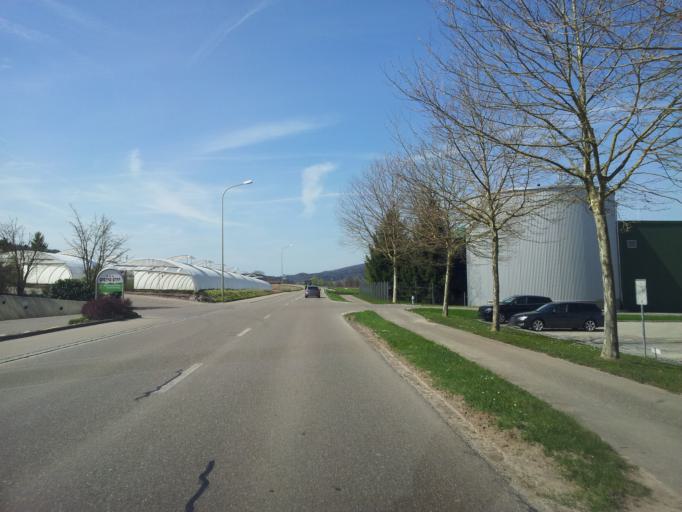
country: CH
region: Zurich
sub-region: Bezirk Dielsdorf
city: Daellikon / Daellikon (Dorf)
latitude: 47.4411
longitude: 8.4326
